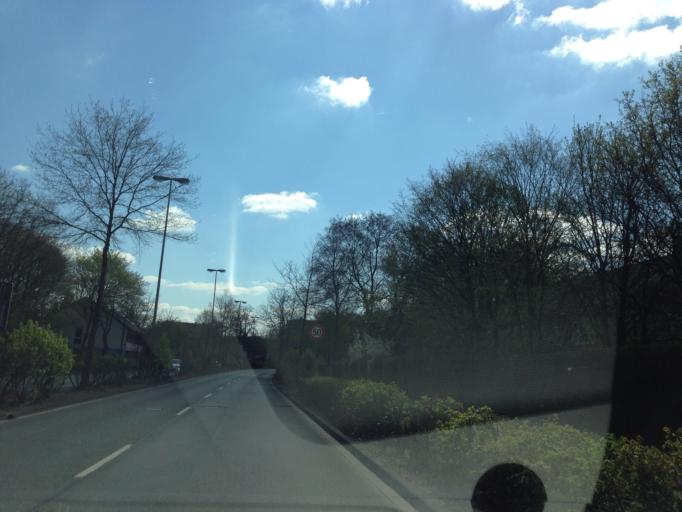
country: DE
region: North Rhine-Westphalia
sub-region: Regierungsbezirk Munster
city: Muenster
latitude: 51.9634
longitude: 7.6018
